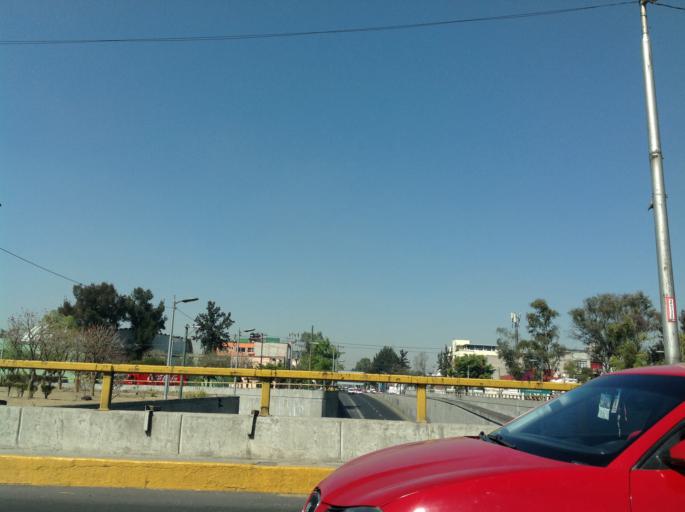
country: MX
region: Mexico City
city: Venustiano Carranza
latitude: 19.4269
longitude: -99.0926
